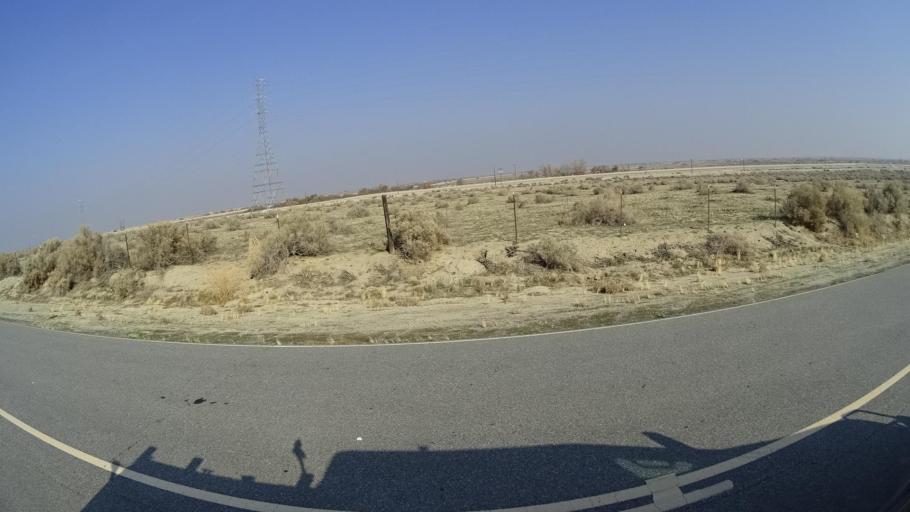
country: US
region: California
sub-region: Kern County
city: Buttonwillow
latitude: 35.2859
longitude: -119.3346
